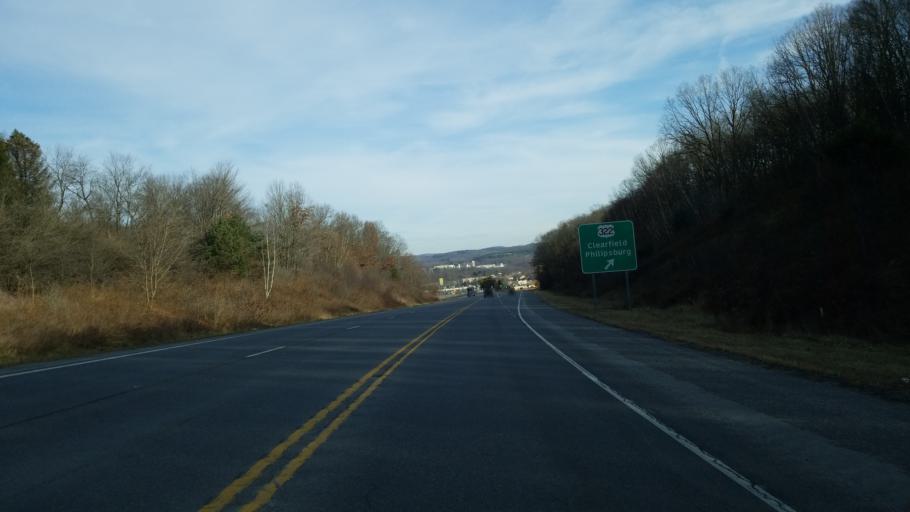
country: US
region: Pennsylvania
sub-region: Clearfield County
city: Clearfield
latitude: 41.0216
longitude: -78.4236
